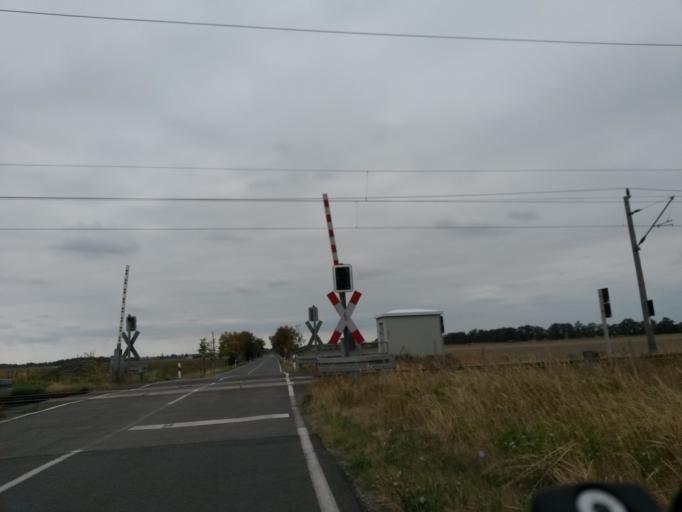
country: DE
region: Saxony-Anhalt
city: Muhlanger
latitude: 51.8495
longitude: 12.7698
